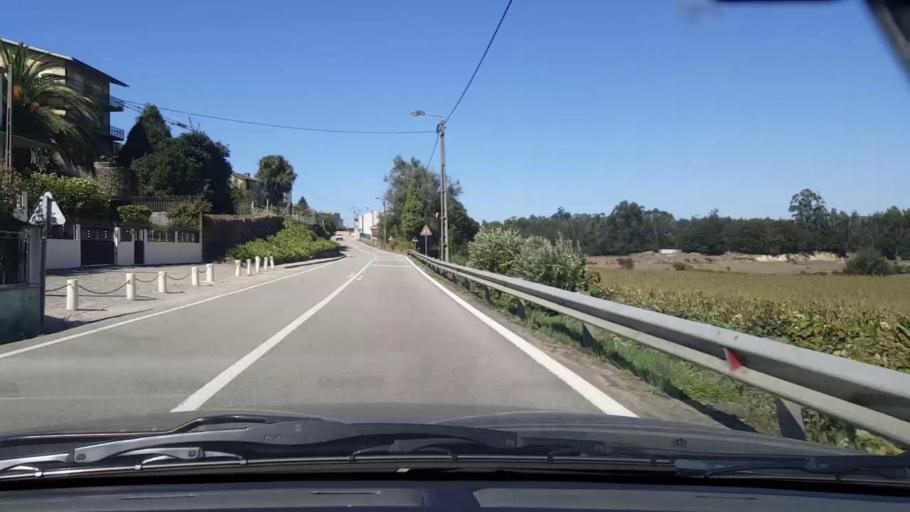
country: PT
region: Porto
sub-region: Maia
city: Gemunde
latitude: 41.3387
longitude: -8.6370
